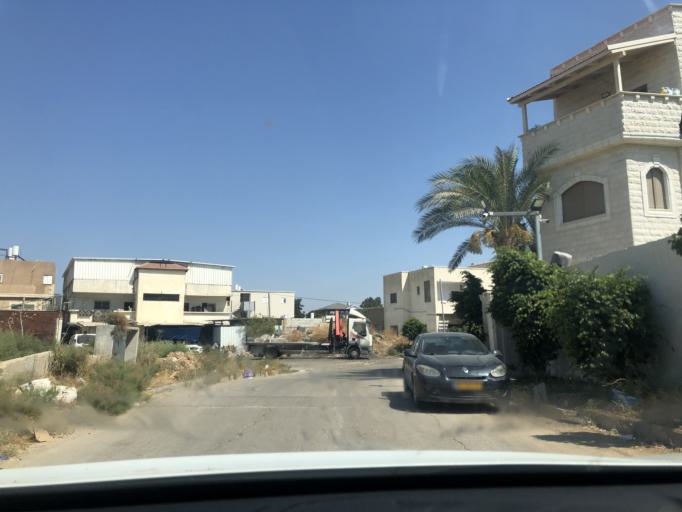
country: IL
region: Central District
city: Lod
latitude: 31.9539
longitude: 34.8765
